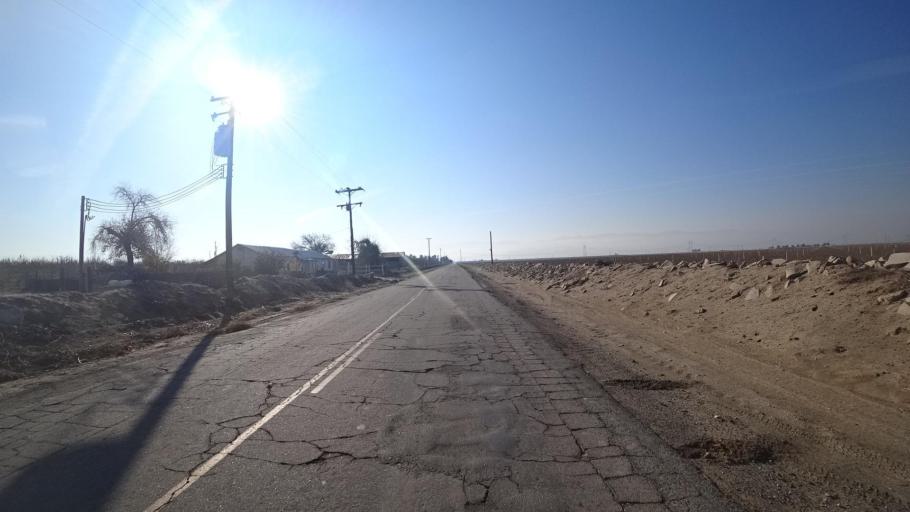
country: US
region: California
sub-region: Kern County
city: Weedpatch
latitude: 35.1364
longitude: -118.9677
